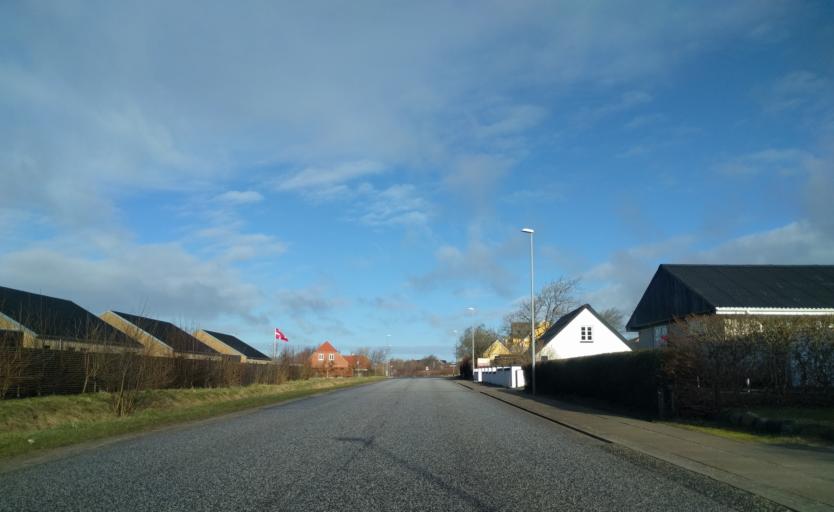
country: DK
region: North Denmark
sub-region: Alborg Kommune
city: Svenstrup
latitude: 57.0168
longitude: 9.8756
